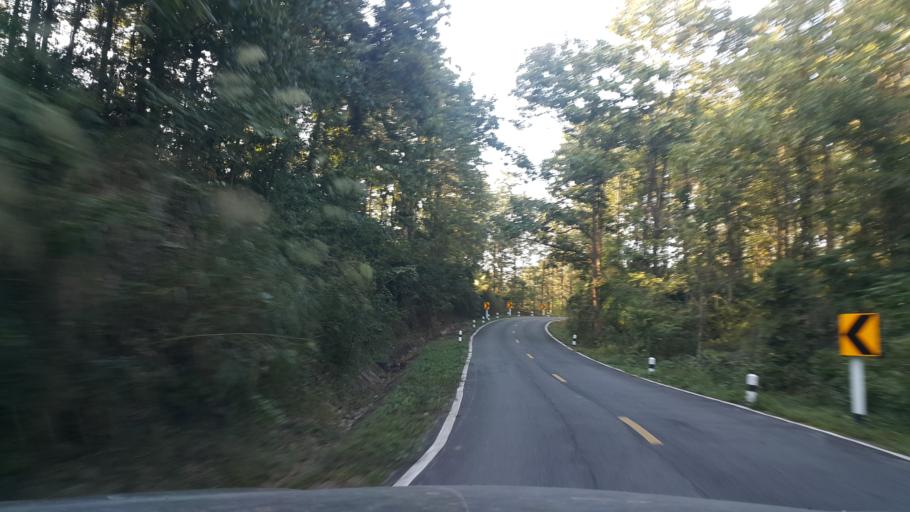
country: TH
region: Lampang
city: Hang Chat
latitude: 18.3502
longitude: 99.2502
